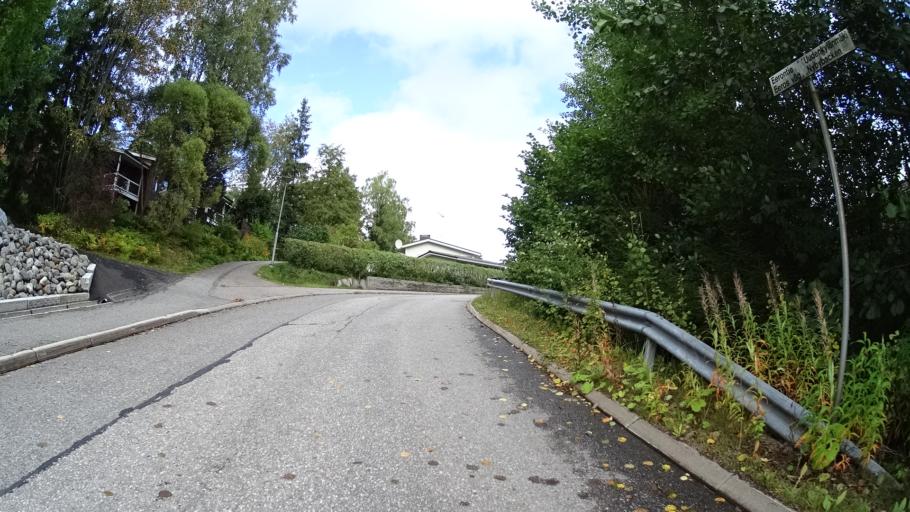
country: FI
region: Uusimaa
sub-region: Helsinki
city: Kauniainen
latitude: 60.1903
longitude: 24.7555
